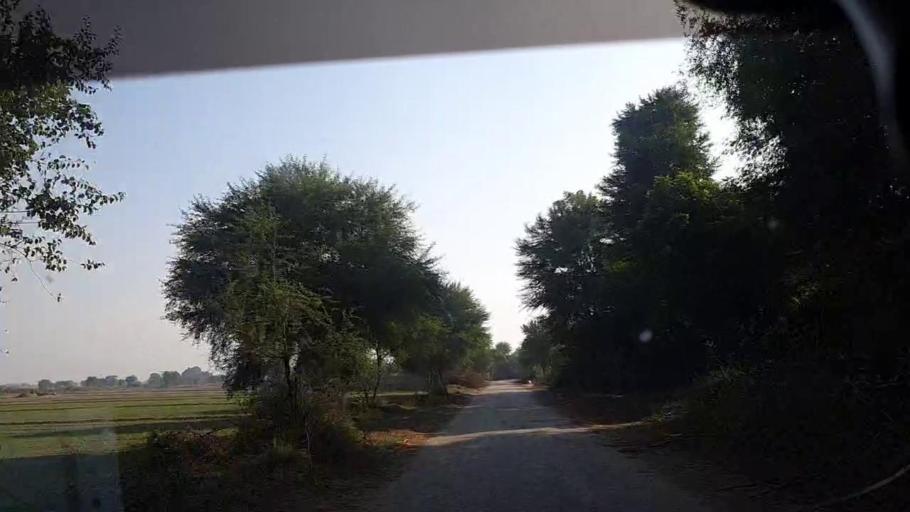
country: PK
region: Sindh
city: Hingorja
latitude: 27.2231
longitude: 68.2700
